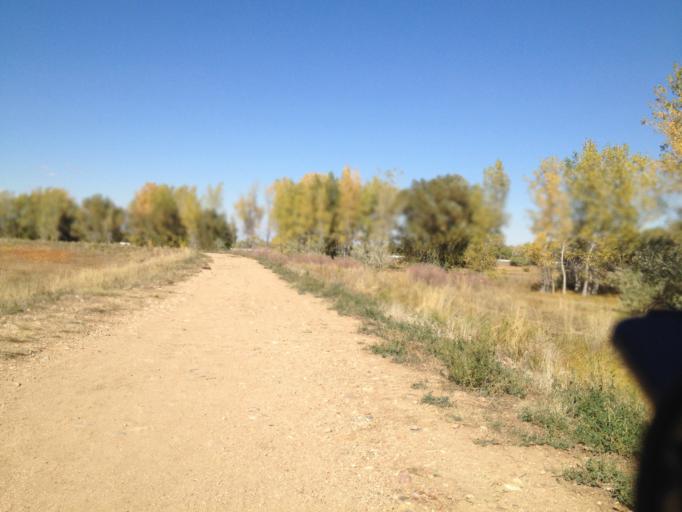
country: US
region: Colorado
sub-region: Boulder County
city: Boulder
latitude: 39.9762
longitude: -105.2251
